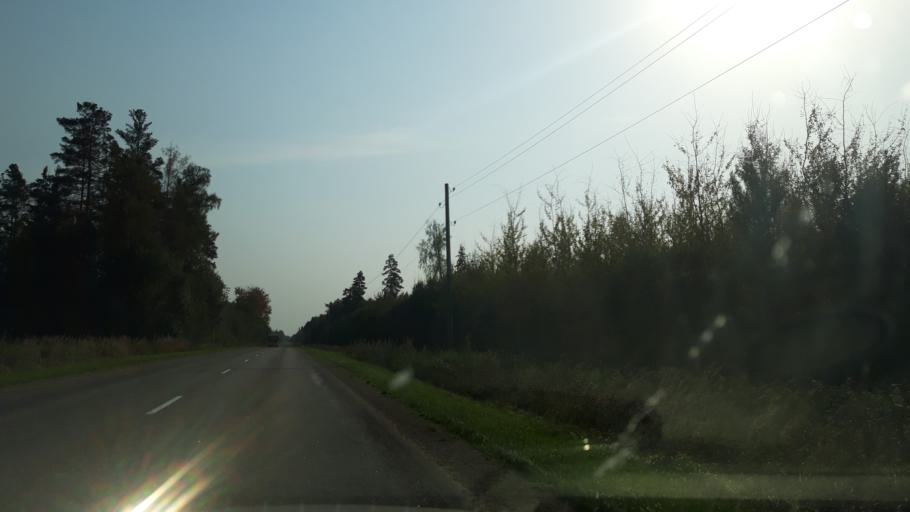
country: LV
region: Burtnieki
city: Matisi
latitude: 57.6457
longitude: 25.2431
